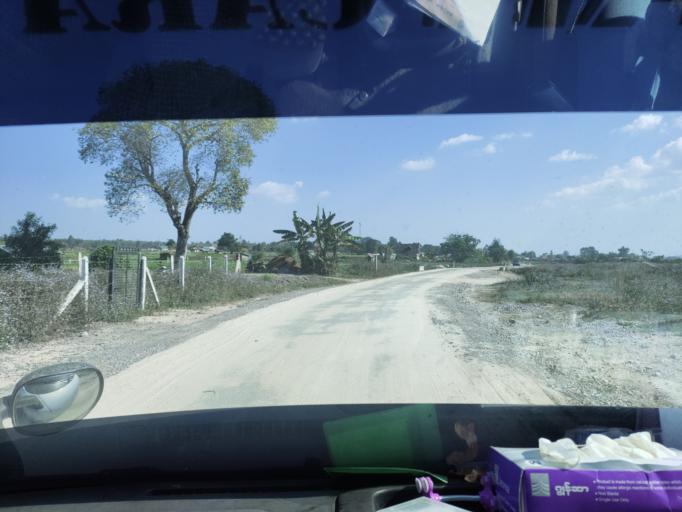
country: MM
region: Mandalay
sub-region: Pyin Oo Lwin District
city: Pyin Oo Lwin
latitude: 22.0667
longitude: 96.5311
